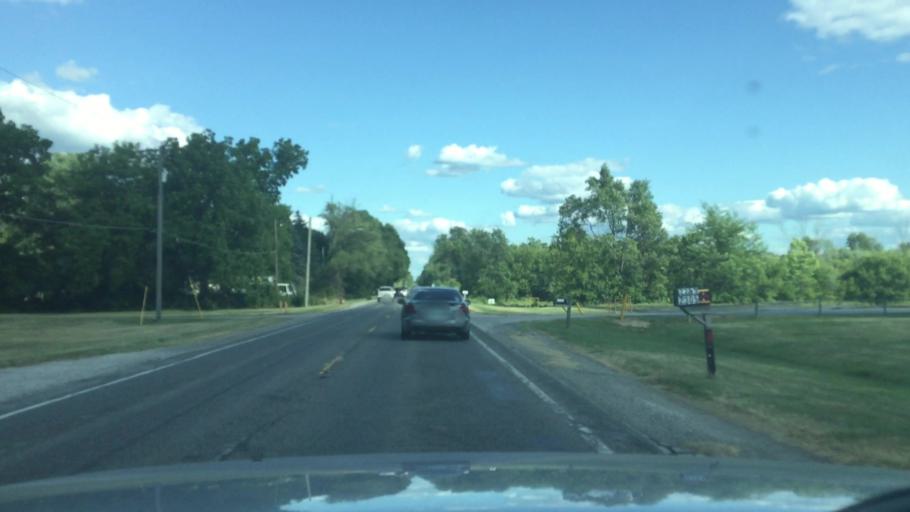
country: US
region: Michigan
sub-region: Saginaw County
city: Saginaw
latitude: 43.3889
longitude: -83.9321
